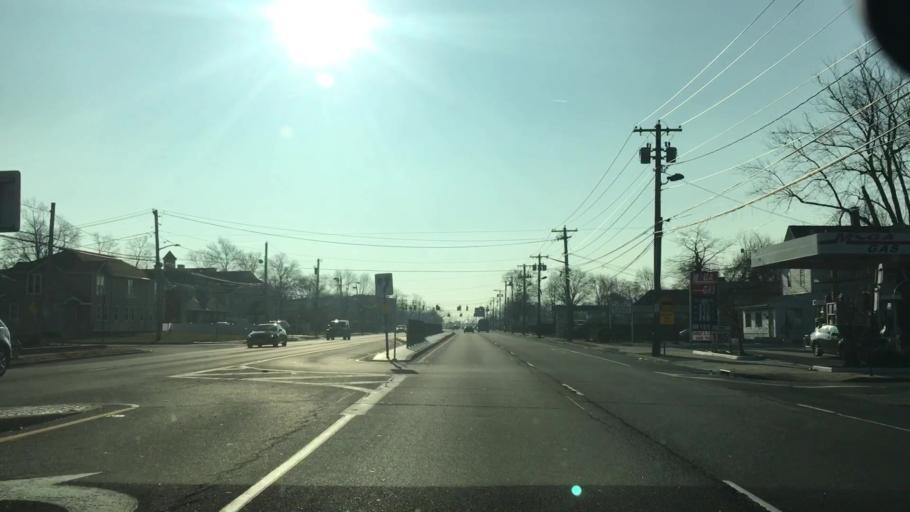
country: US
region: New York
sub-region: Suffolk County
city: North Amityville
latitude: 40.6969
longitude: -73.4250
